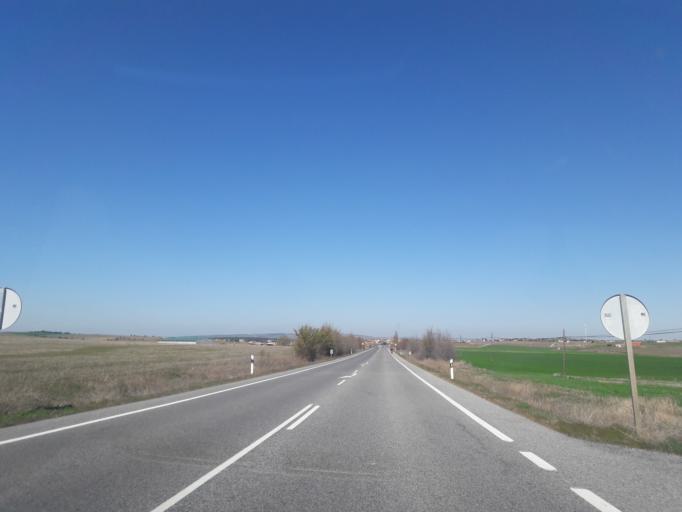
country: ES
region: Castille and Leon
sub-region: Provincia de Salamanca
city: Mozarbez
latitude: 40.8479
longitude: -5.6445
